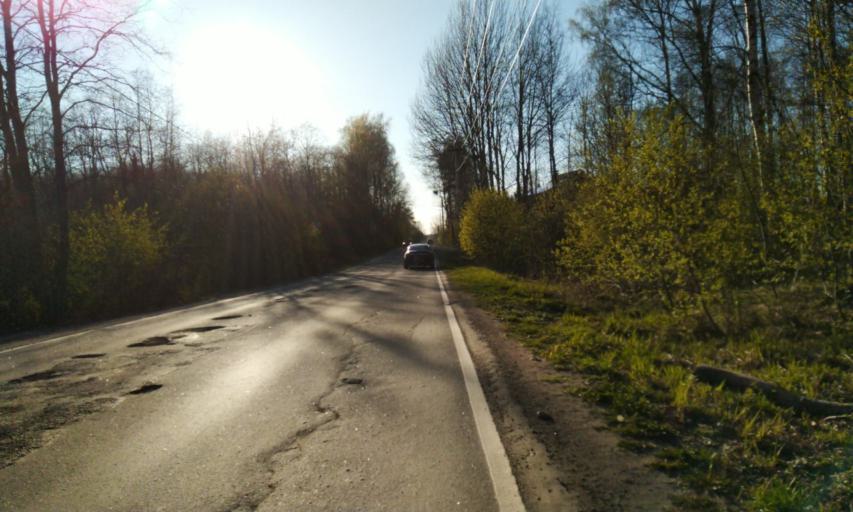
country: RU
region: Leningrad
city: Toksovo
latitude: 60.1408
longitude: 30.5390
